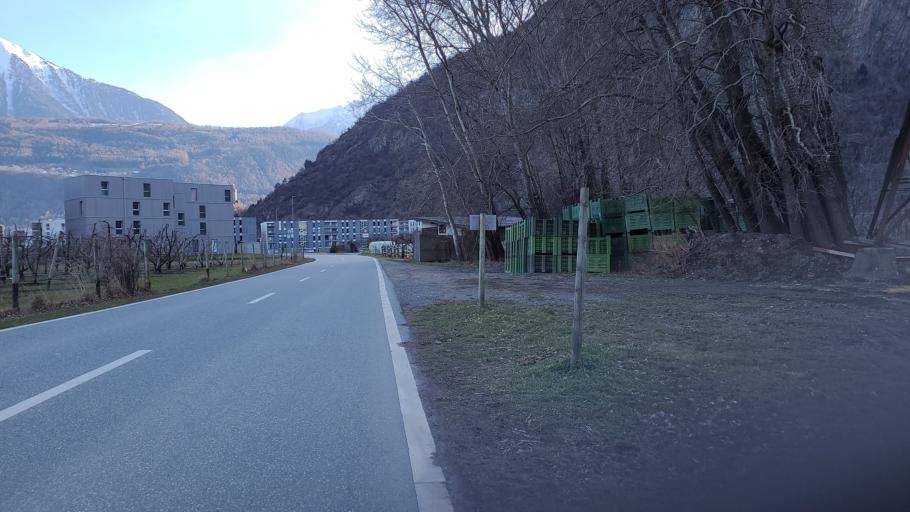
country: CH
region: Valais
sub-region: Martigny District
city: Martigny-Ville
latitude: 46.1158
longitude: 7.0661
